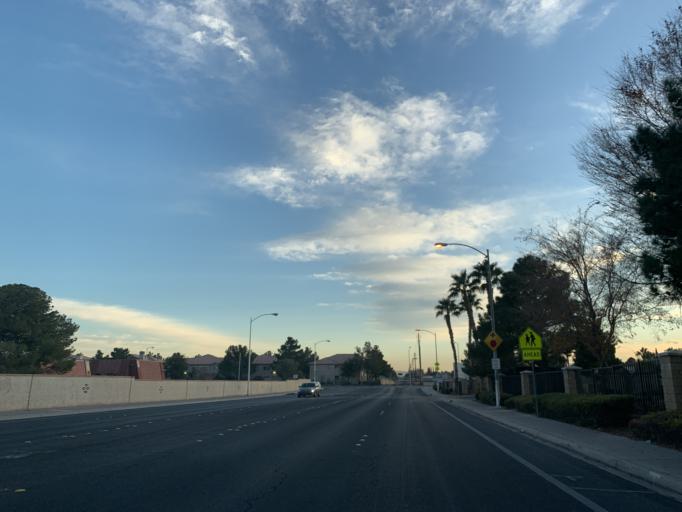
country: US
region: Nevada
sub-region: Clark County
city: Spring Valley
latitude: 36.1089
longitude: -115.2166
